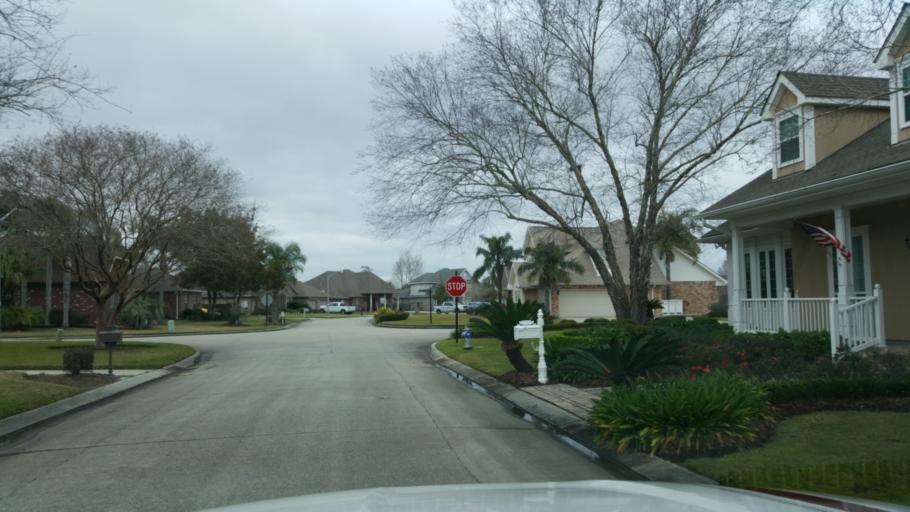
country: US
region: Louisiana
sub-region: Jefferson Parish
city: Woodmere
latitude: 29.8753
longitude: -90.0801
